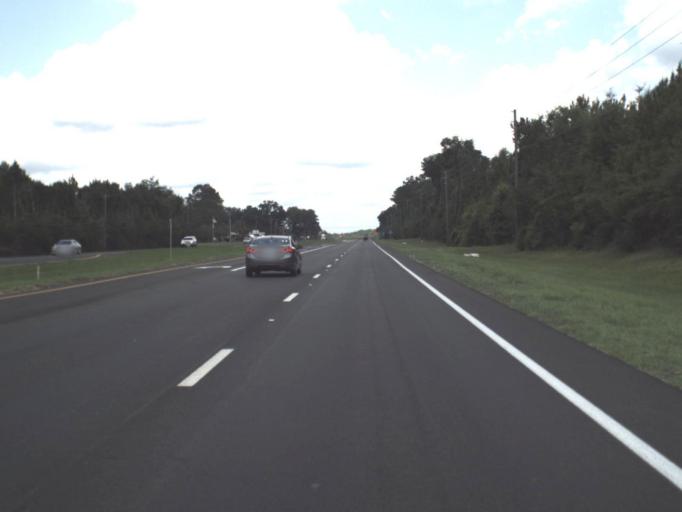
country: US
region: Florida
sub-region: Alachua County
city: Alachua
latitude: 29.7673
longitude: -82.4165
